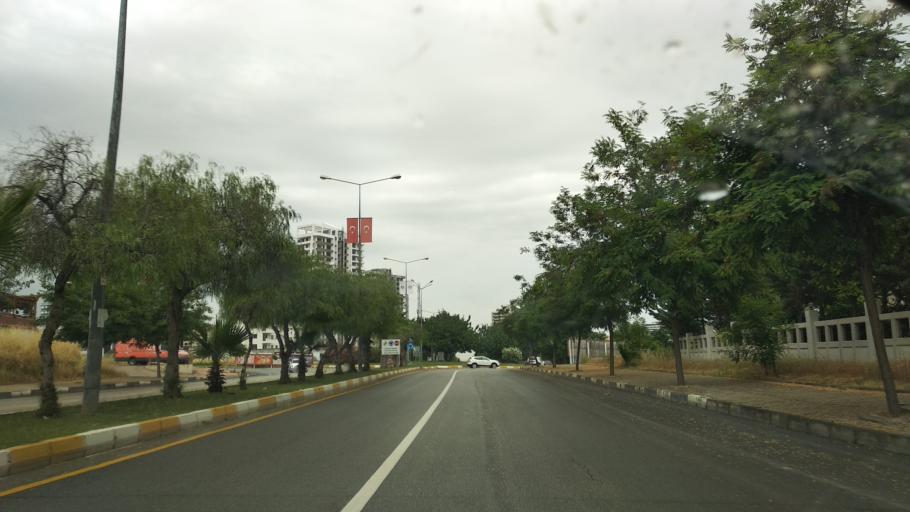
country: TR
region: Mersin
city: Mercin
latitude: 36.7954
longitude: 34.5853
